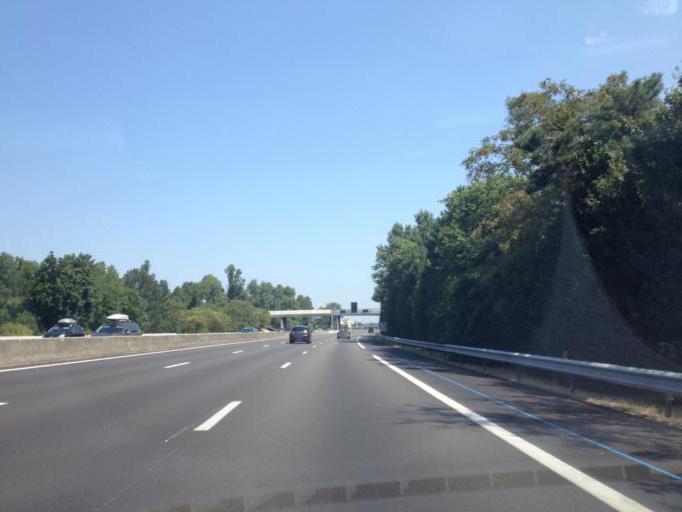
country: FR
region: Rhone-Alpes
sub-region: Departement de l'Ardeche
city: Guilherand-Granges
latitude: 44.9221
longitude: 4.8776
